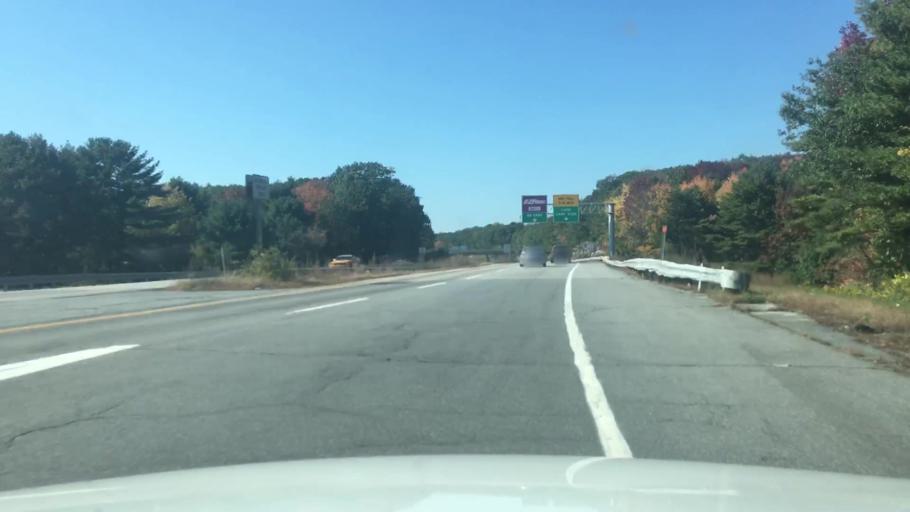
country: US
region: Maine
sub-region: Cumberland County
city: Falmouth
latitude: 43.7322
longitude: -70.2330
